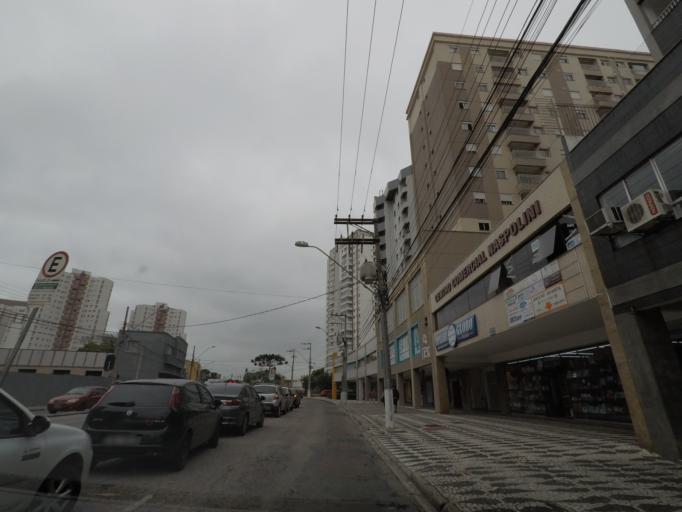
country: BR
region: Parana
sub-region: Curitiba
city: Curitiba
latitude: -25.4679
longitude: -49.2935
